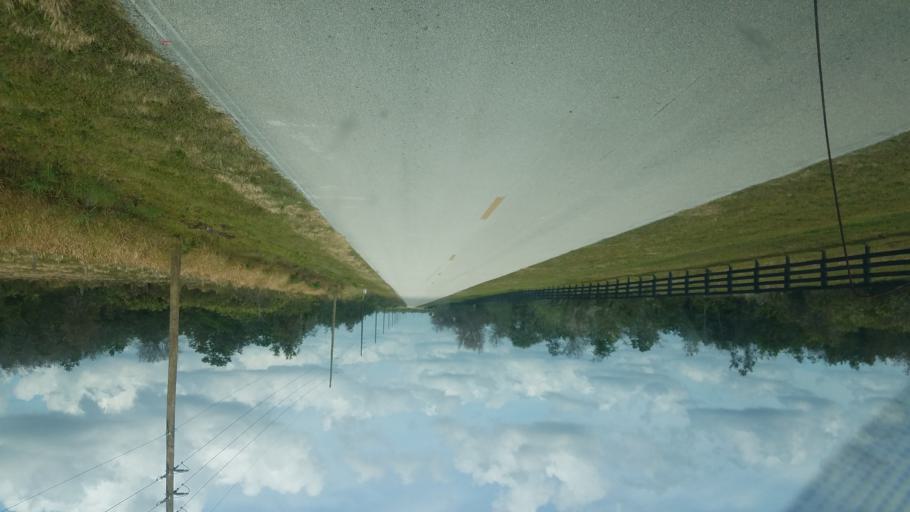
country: US
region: Florida
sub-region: Okeechobee County
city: Cypress Quarters
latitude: 27.4631
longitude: -80.7708
